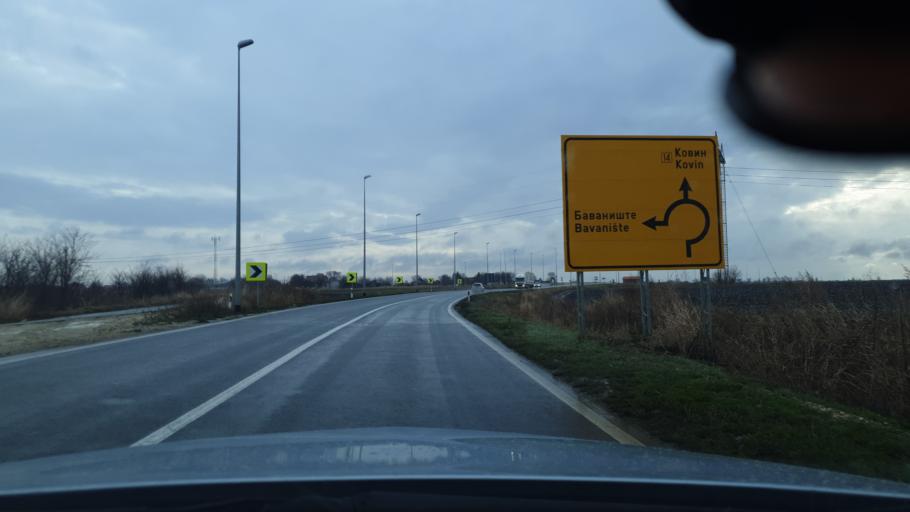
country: RS
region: Autonomna Pokrajina Vojvodina
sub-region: Juznobanatski Okrug
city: Kovin
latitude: 44.8257
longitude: 20.8491
